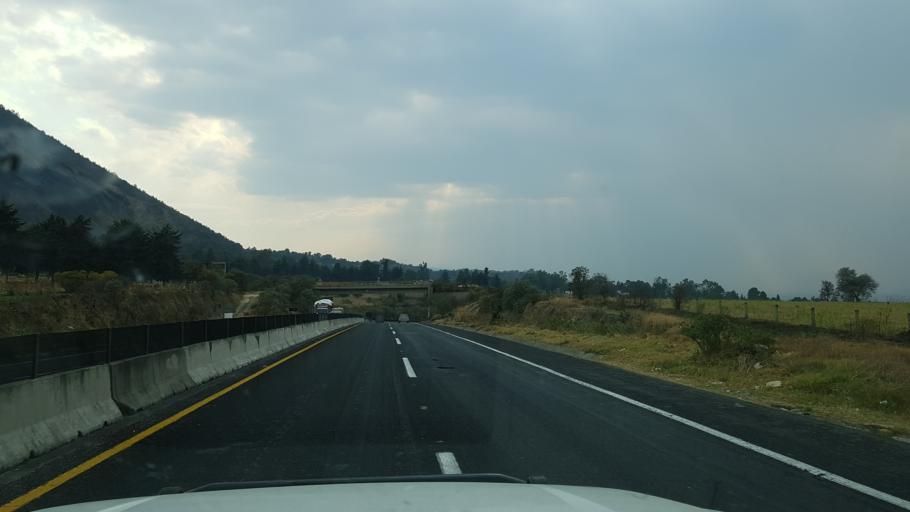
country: MX
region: Mexico
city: Tlalmanalco de Velazquez
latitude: 19.1954
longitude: -98.8088
